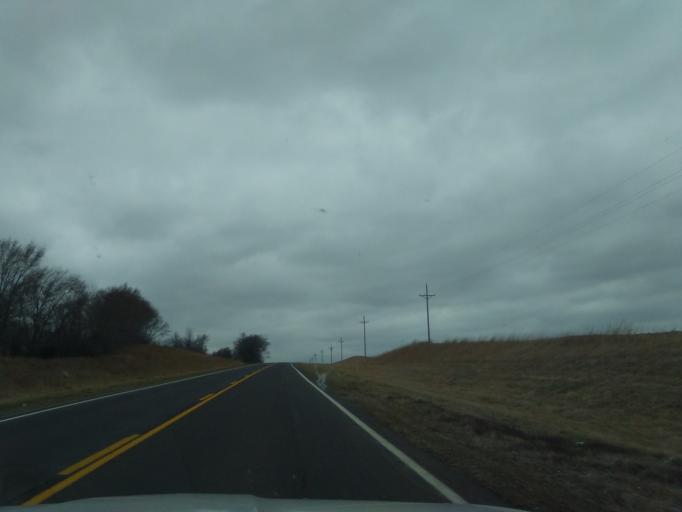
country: US
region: Nebraska
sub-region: Richardson County
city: Falls City
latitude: 40.0577
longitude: -95.4542
